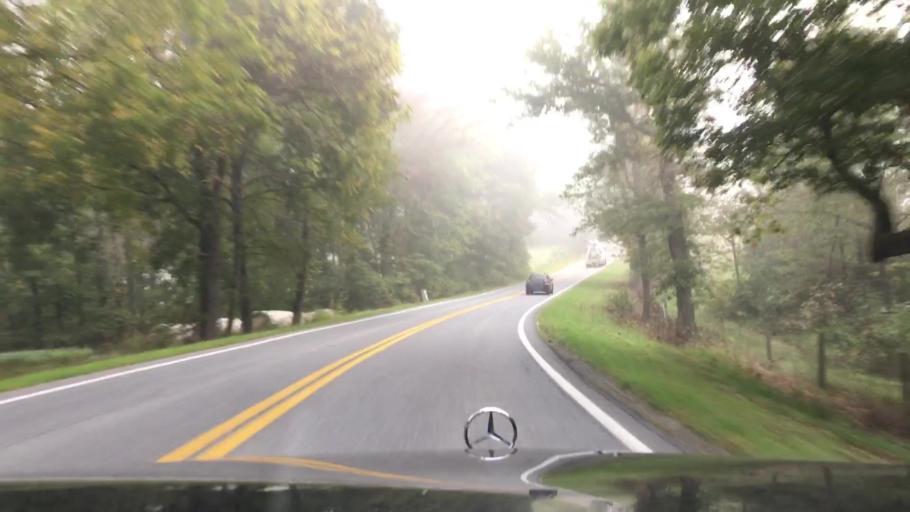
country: US
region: Virginia
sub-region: Campbell County
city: Timberlake
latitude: 37.2190
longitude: -79.2916
